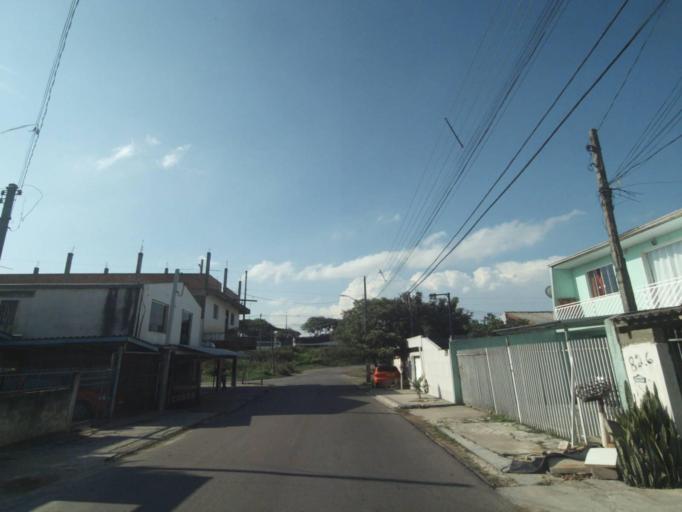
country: BR
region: Parana
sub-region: Araucaria
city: Araucaria
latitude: -25.5256
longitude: -49.3351
